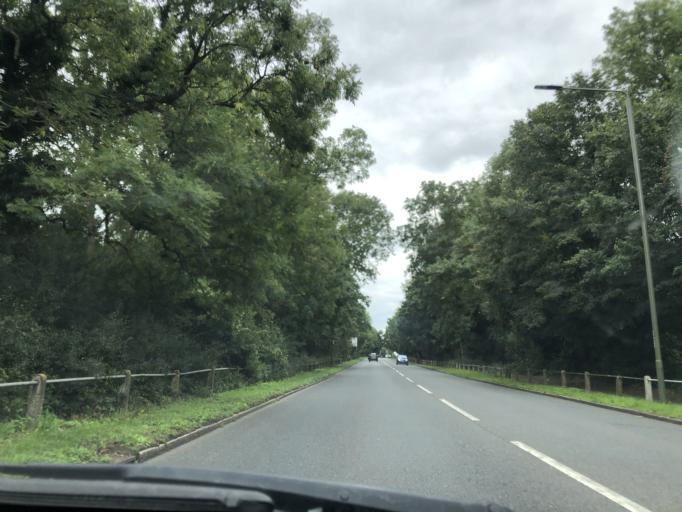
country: GB
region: England
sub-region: Greater London
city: Orpington
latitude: 51.3609
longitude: 0.1180
